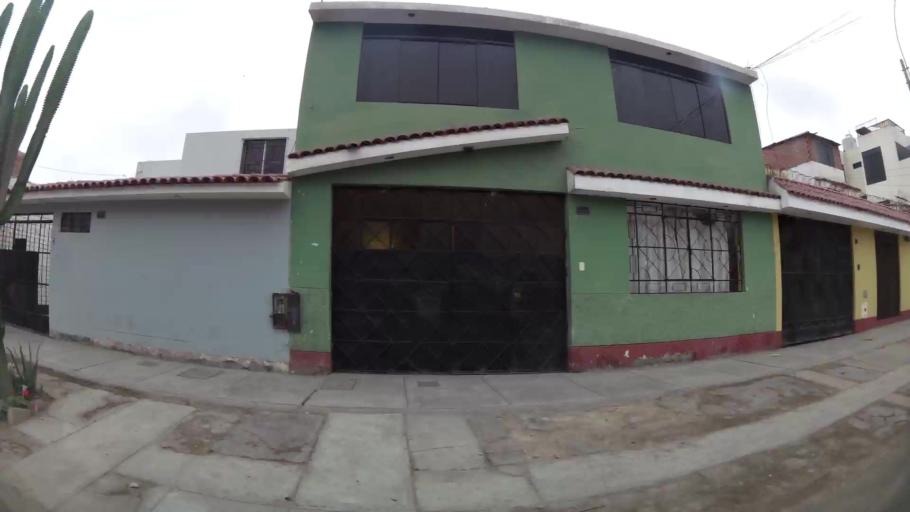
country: PE
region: Callao
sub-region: Callao
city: Callao
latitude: -12.0528
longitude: -77.1117
